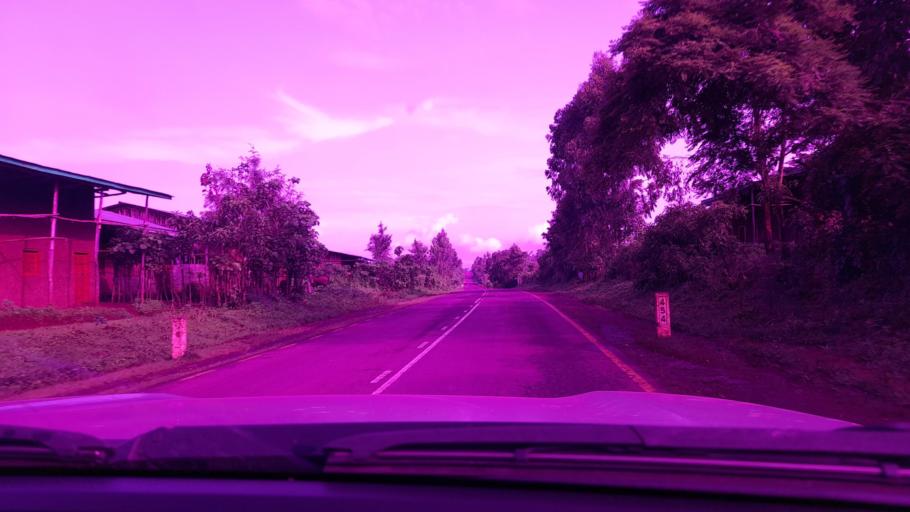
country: ET
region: Oromiya
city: Bedele
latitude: 8.1828
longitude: 36.4533
